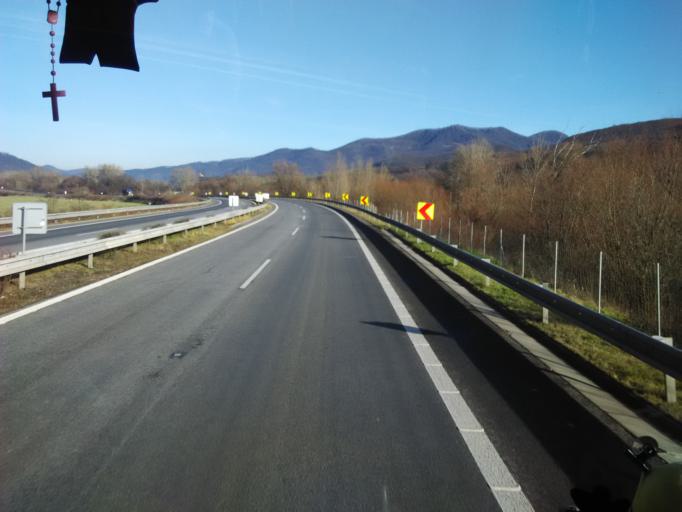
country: SK
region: Banskobystricky
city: Nova Bana
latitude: 48.4184
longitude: 18.6623
